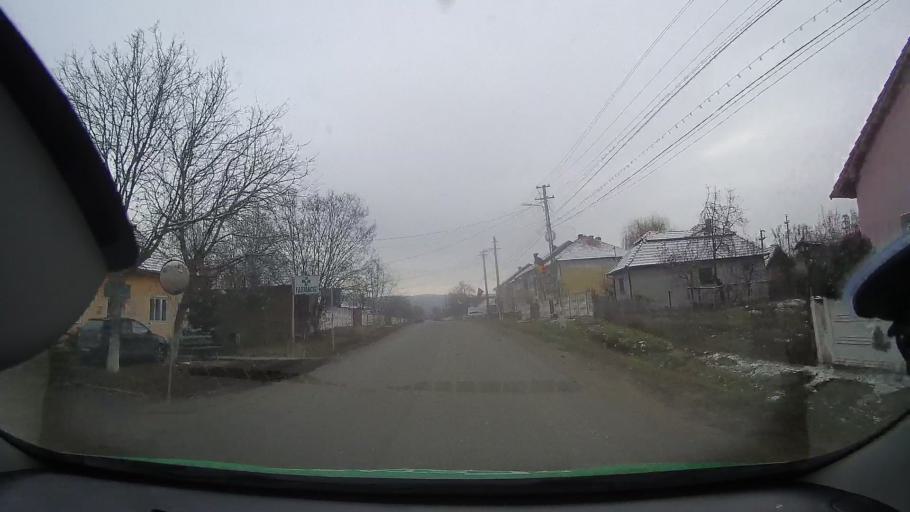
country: RO
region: Alba
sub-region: Comuna Farau
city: Farau
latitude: 46.3398
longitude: 23.9969
